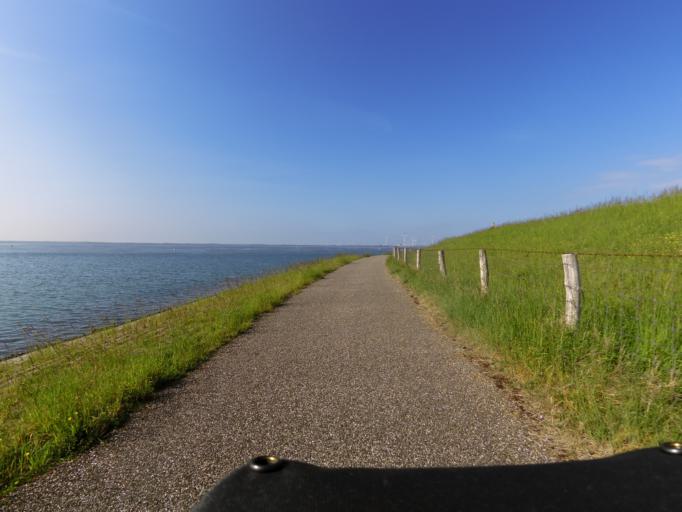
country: NL
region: Zeeland
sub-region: Schouwen-Duiveland
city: Burgh
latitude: 51.6737
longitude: 3.7532
